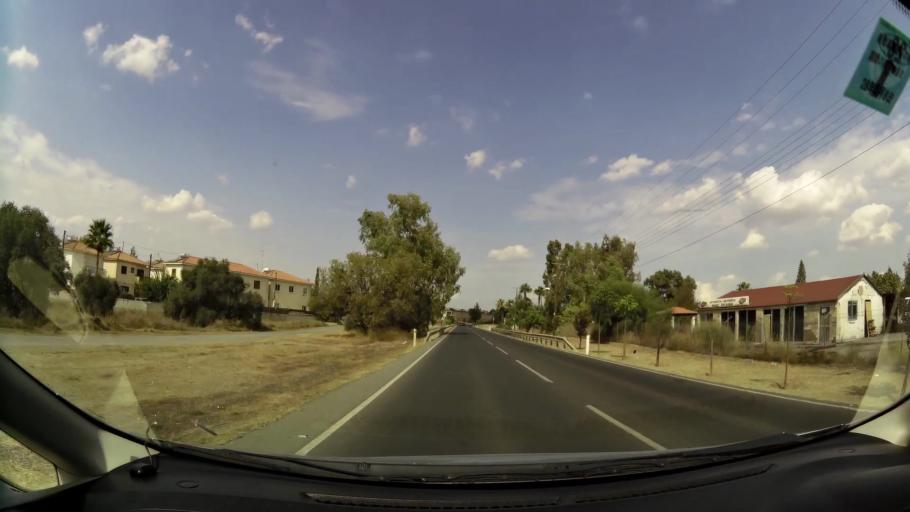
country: CY
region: Lefkosia
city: Tseri
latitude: 35.0900
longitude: 33.3278
